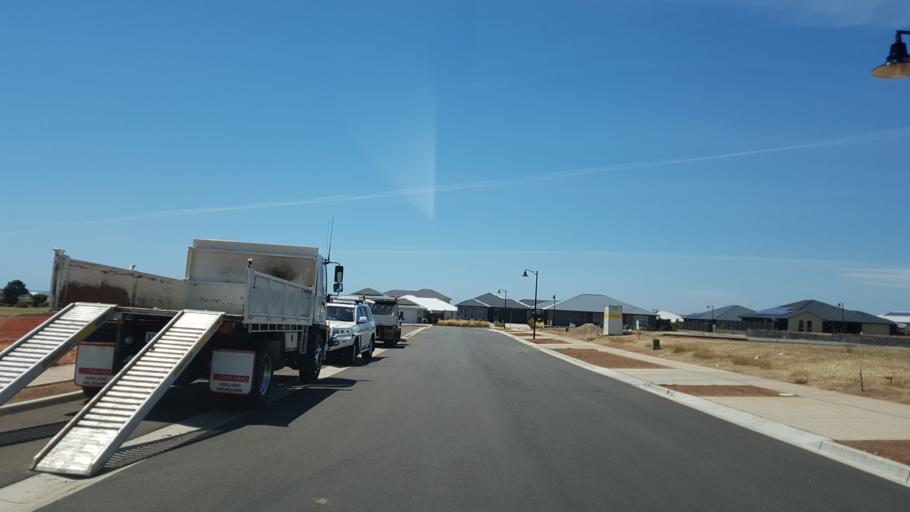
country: AU
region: South Australia
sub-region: Onkaparinga
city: Moana
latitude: -35.2187
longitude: 138.4756
